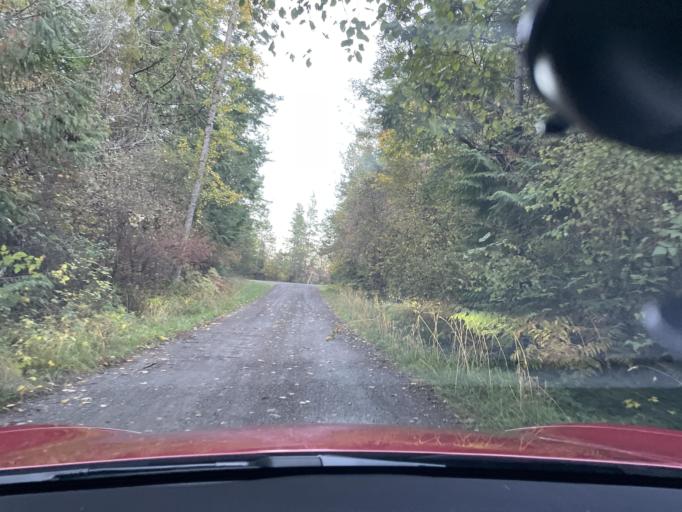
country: US
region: Washington
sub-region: San Juan County
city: Friday Harbor
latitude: 48.6147
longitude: -123.1392
